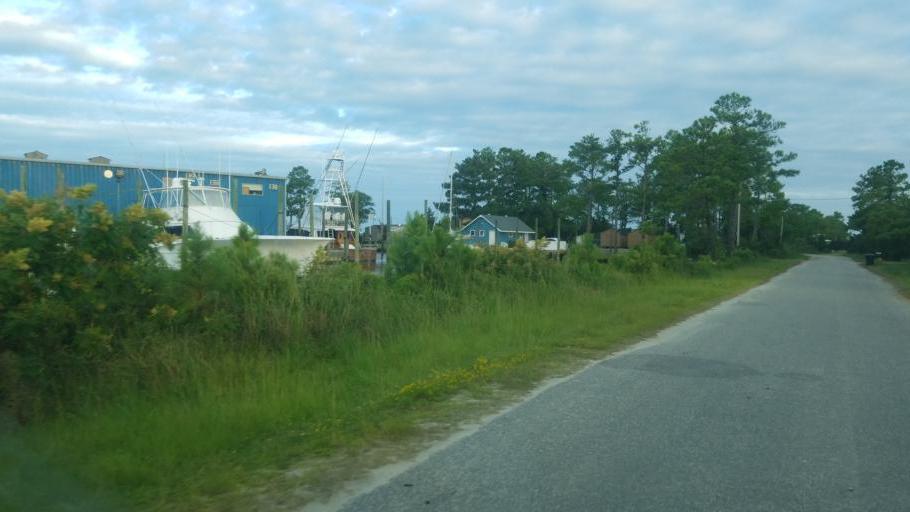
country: US
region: North Carolina
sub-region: Dare County
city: Wanchese
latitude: 35.8447
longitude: -75.6542
